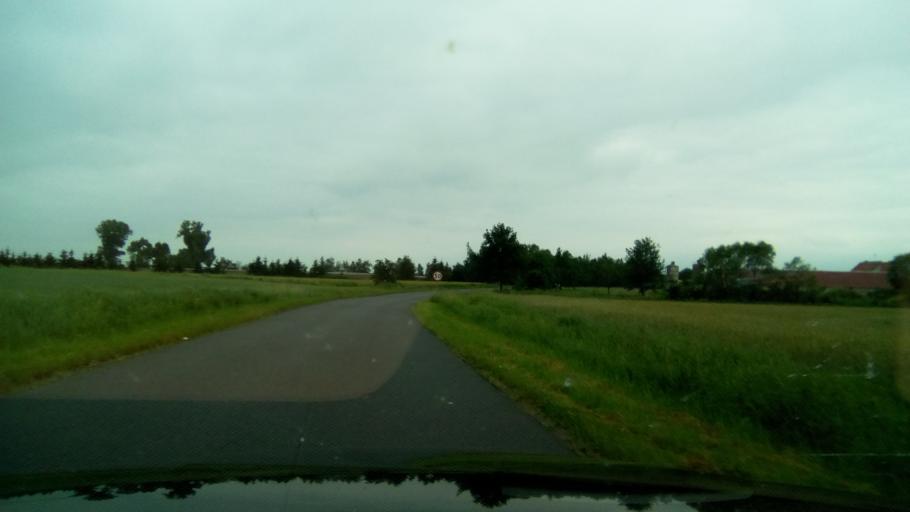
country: PL
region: Greater Poland Voivodeship
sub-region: Powiat gnieznienski
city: Czerniejewo
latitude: 52.4738
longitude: 17.5164
